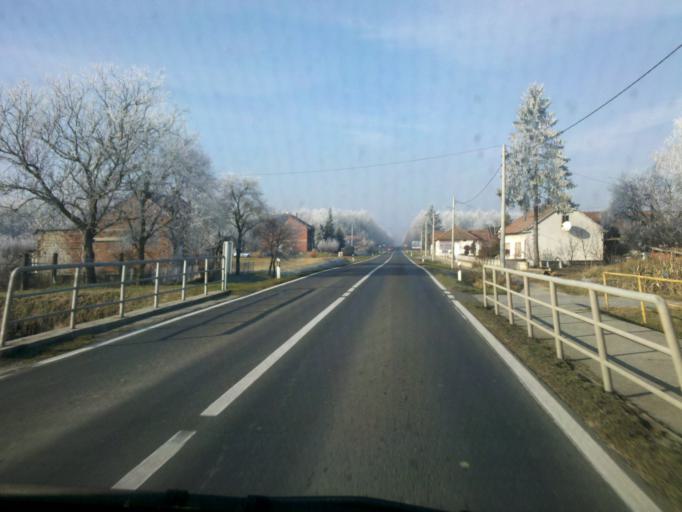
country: HR
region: Koprivnicko-Krizevacka
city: Kalinovac
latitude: 45.9904
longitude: 17.1319
